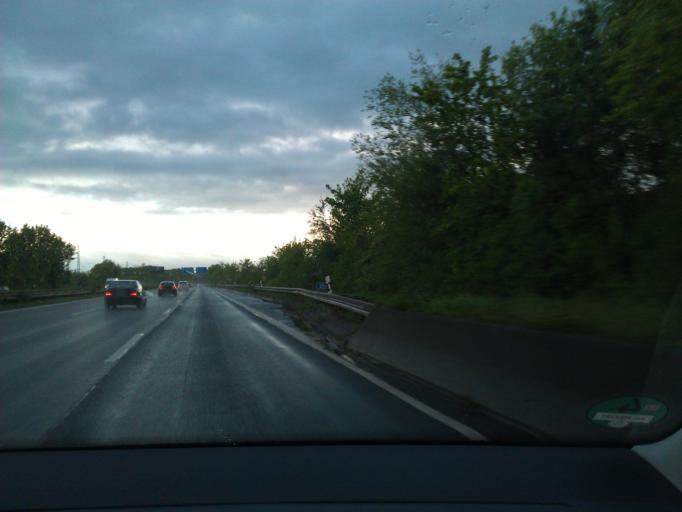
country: DE
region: North Rhine-Westphalia
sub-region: Regierungsbezirk Koln
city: Troisdorf
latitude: 50.7761
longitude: 7.1466
